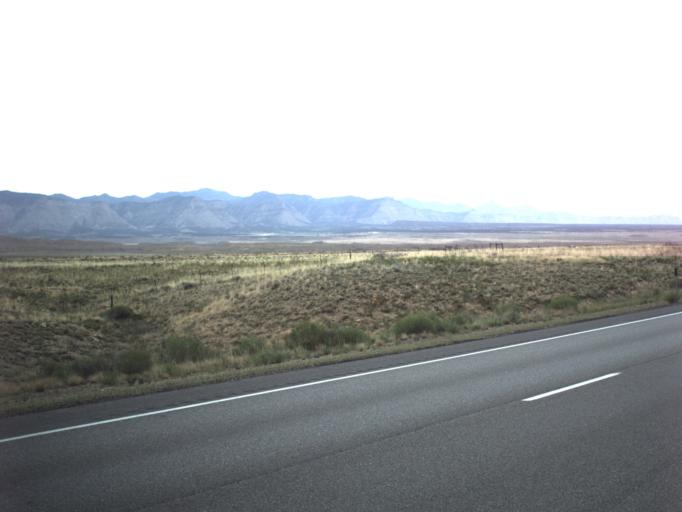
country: US
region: Utah
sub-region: Carbon County
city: East Carbon City
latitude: 39.4884
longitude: -110.5168
